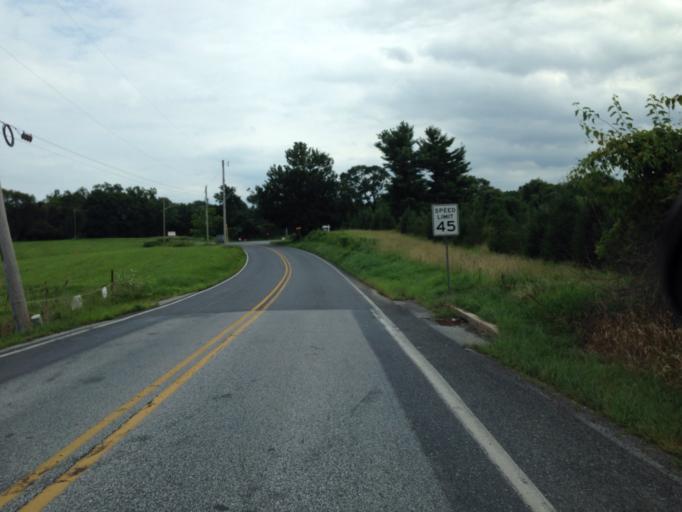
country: US
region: Delaware
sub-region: New Castle County
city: Newark
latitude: 39.7224
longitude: -75.7910
